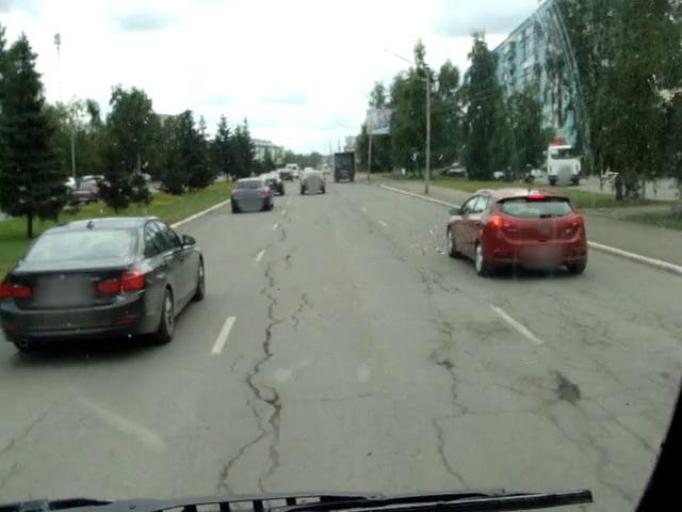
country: RU
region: Altai Krai
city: Biysk
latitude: 52.5457
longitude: 85.2147
